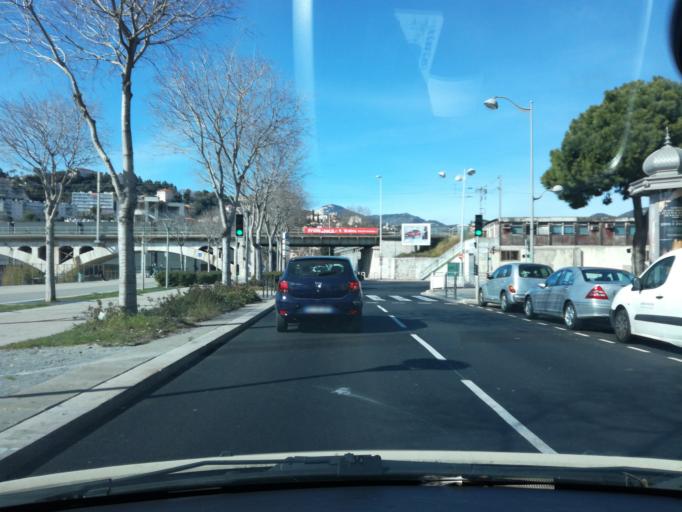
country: FR
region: Provence-Alpes-Cote d'Azur
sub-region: Departement des Alpes-Maritimes
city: Saint-Andre-de-la-Roche
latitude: 43.7137
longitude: 7.2837
